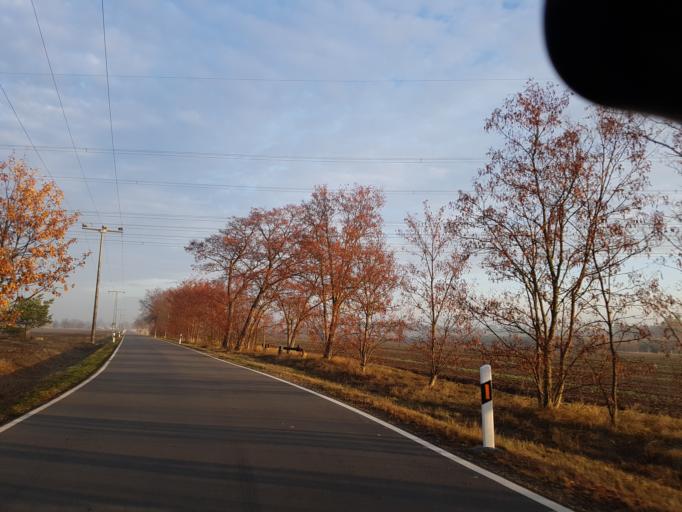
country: DE
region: Saxony-Anhalt
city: Elster
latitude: 51.8541
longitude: 12.8451
